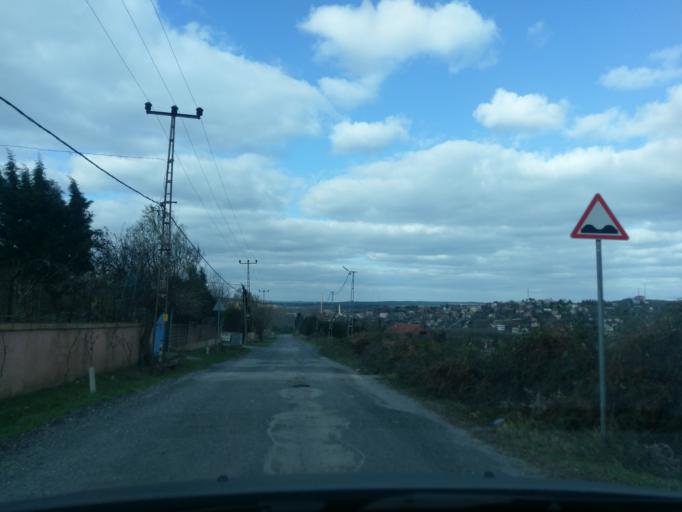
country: TR
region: Istanbul
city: Durusu
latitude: 41.2918
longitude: 28.6841
